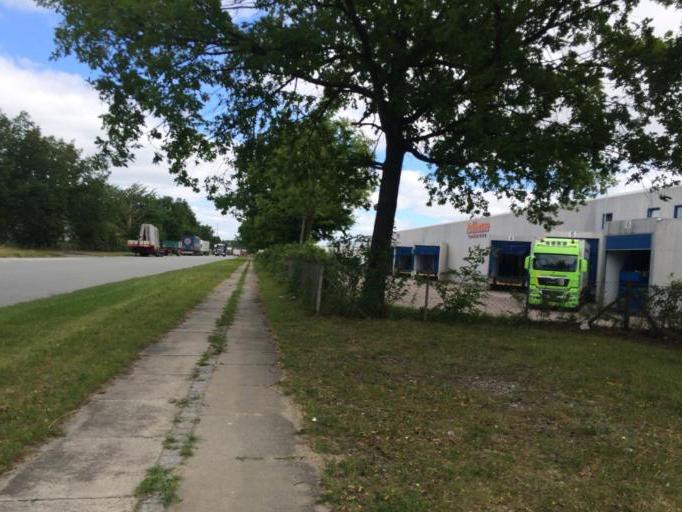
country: DK
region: Capital Region
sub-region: Hvidovre Kommune
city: Hvidovre
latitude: 55.6083
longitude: 12.4684
